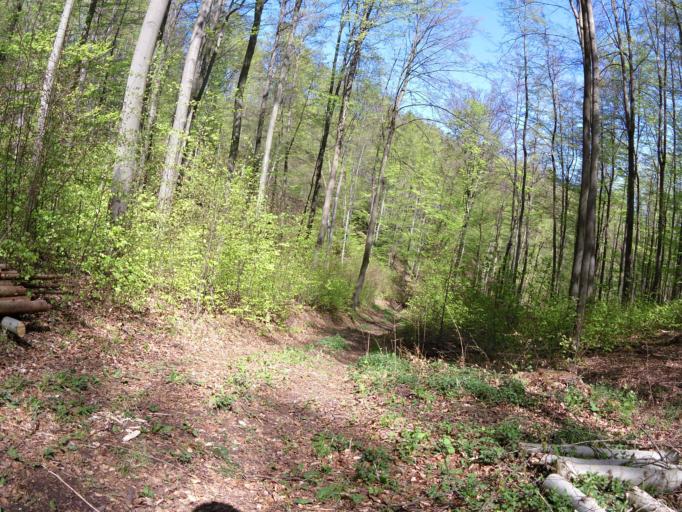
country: DE
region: Thuringia
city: Krauthausen
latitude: 50.9822
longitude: 10.2336
